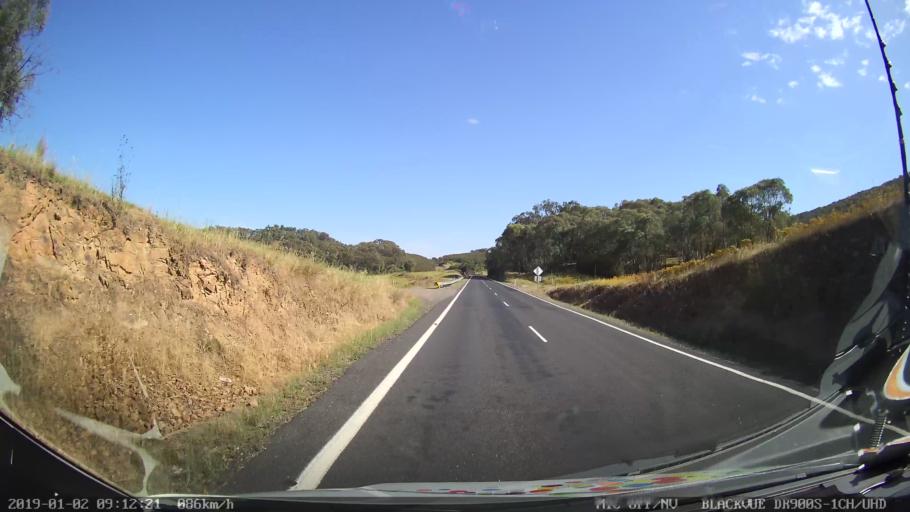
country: AU
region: New South Wales
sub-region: Tumut Shire
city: Tumut
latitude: -35.5015
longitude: 148.2723
